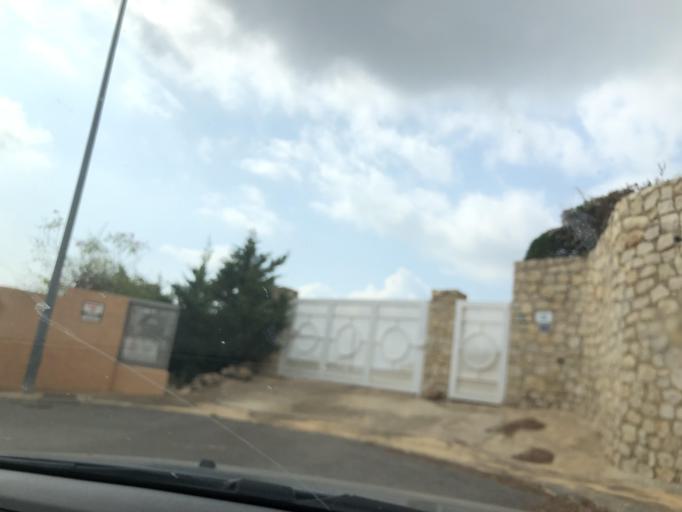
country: ES
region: Valencia
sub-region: Provincia de Alicante
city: Callosa d'En Sarria
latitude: 38.6427
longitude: -0.0723
